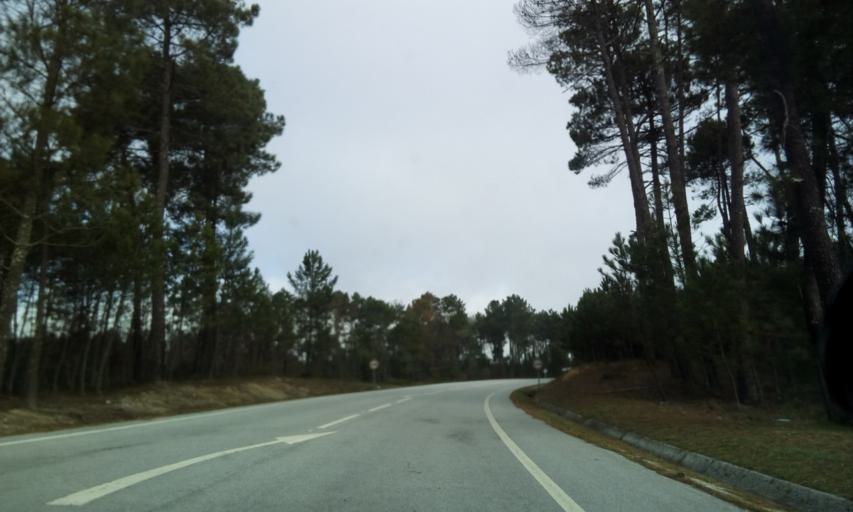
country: PT
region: Guarda
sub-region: Aguiar da Beira
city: Aguiar da Beira
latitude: 40.7501
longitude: -7.5049
